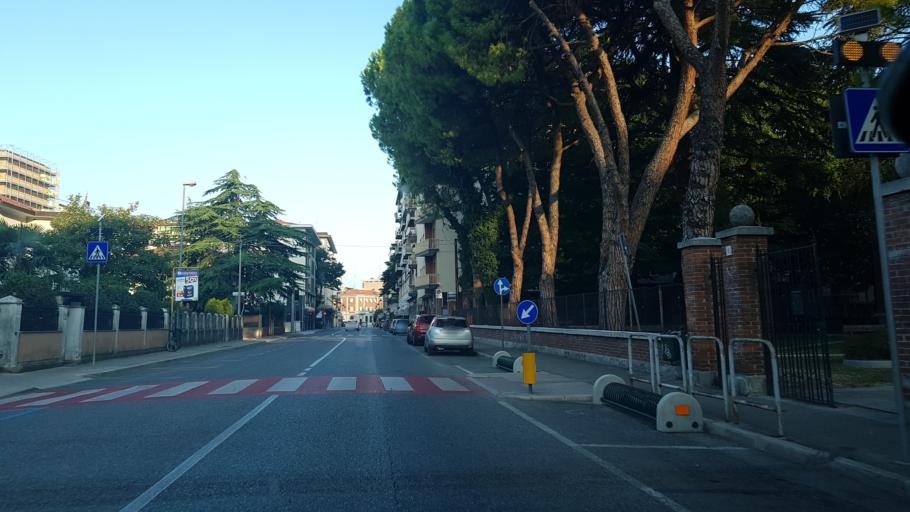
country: IT
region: Friuli Venezia Giulia
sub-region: Provincia di Gorizia
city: Monfalcone
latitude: 45.8071
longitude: 13.5369
